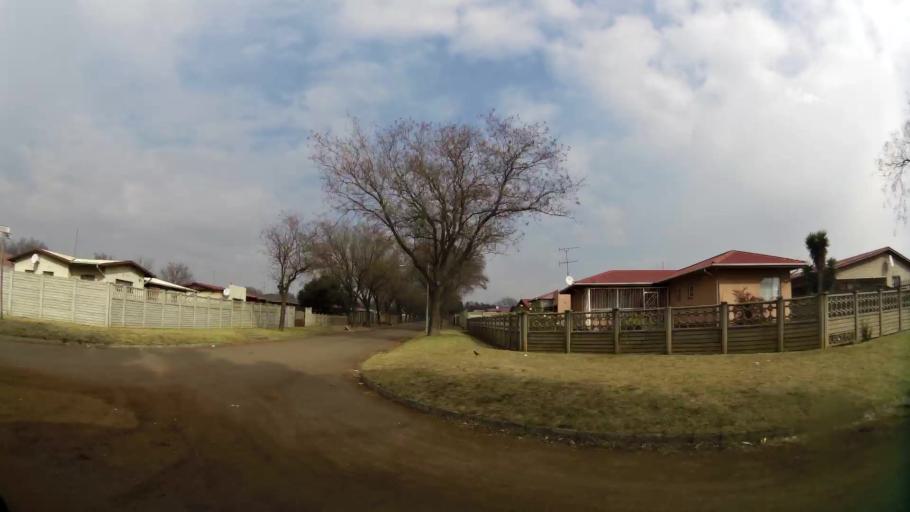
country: ZA
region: Gauteng
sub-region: Sedibeng District Municipality
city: Vanderbijlpark
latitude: -26.6776
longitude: 27.8362
